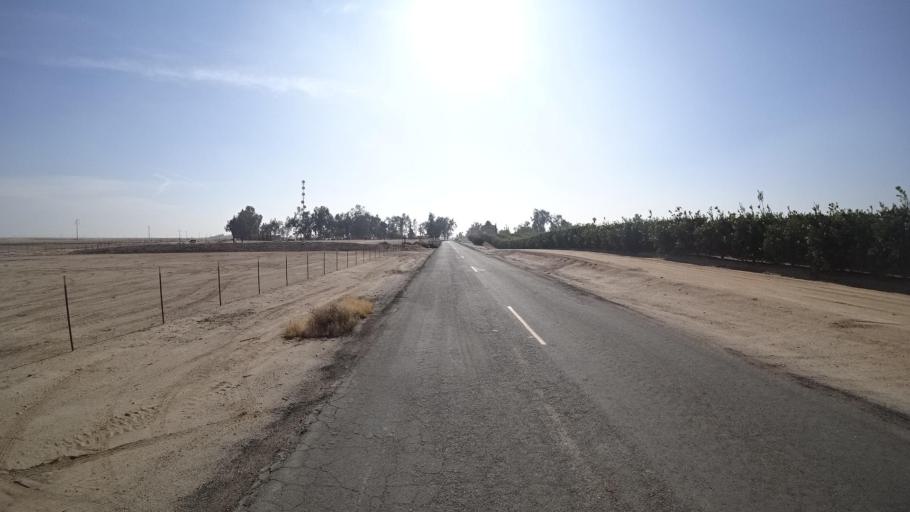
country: US
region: California
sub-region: Kern County
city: Oildale
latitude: 35.5254
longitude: -119.1084
